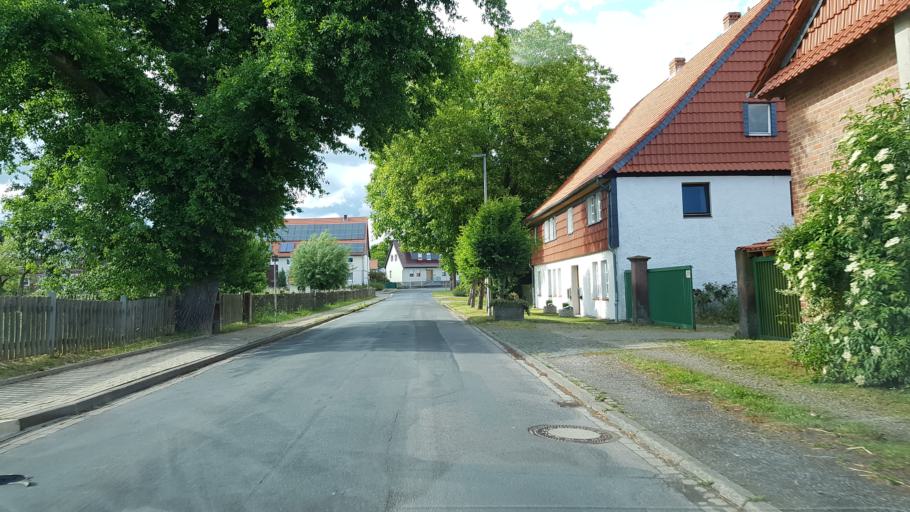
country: DE
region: Lower Saxony
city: Einbeck
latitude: 51.7826
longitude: 9.8984
